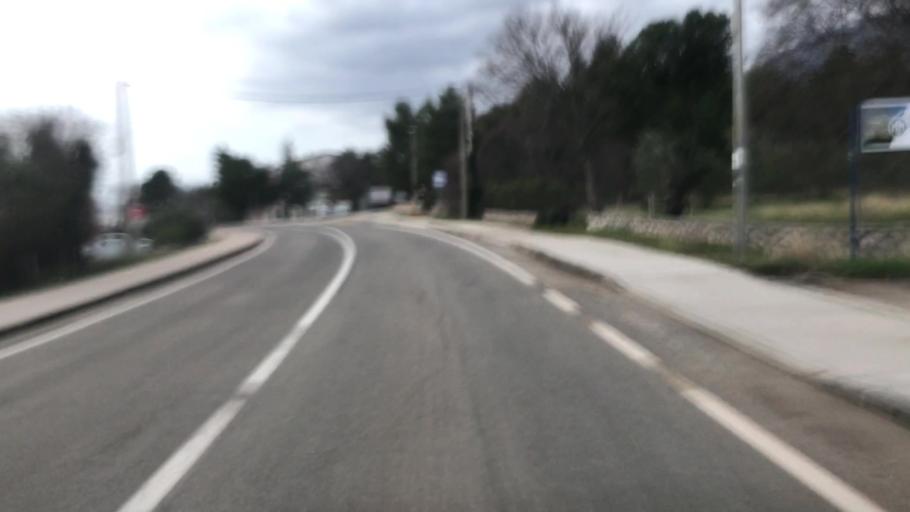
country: HR
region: Zadarska
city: Starigrad
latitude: 44.2881
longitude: 15.4483
